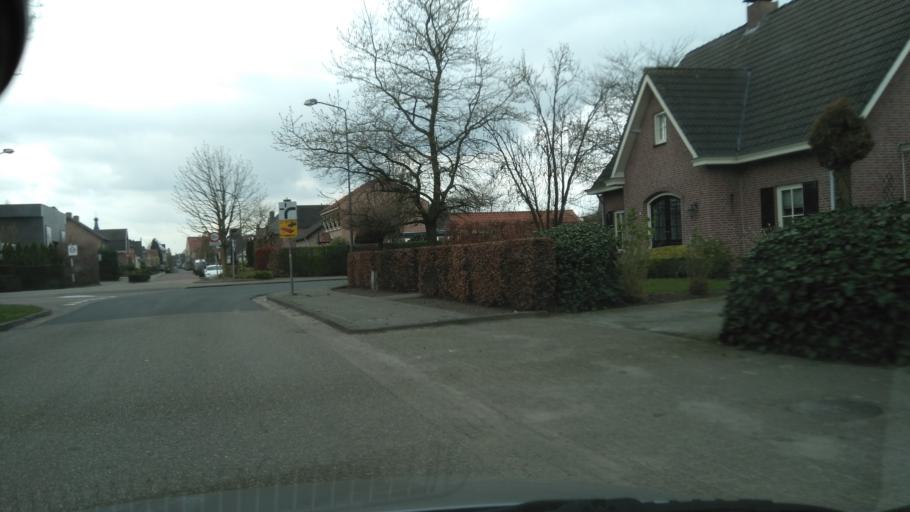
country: NL
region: North Brabant
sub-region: Gemeente Baarle-Nassau
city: Baarle-Nassau
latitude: 51.4460
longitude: 4.9382
